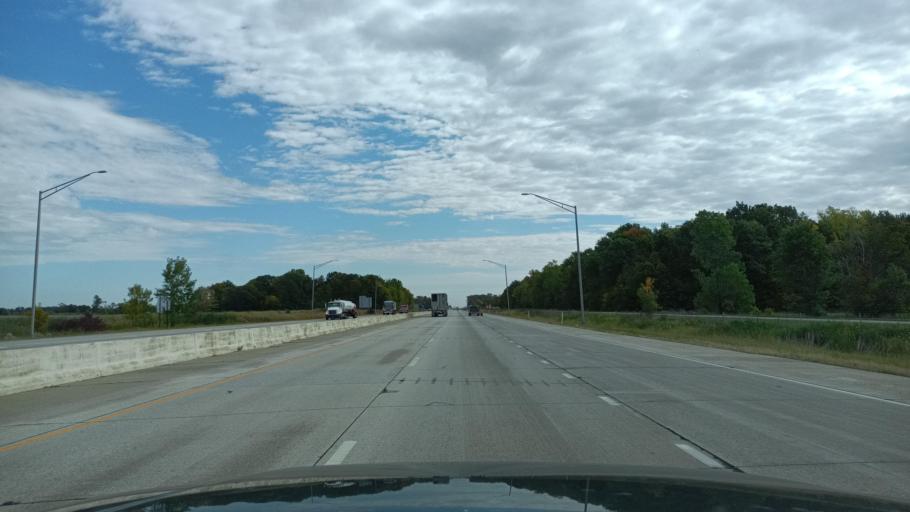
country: US
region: Indiana
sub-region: Wells County
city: Ossian
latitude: 40.9548
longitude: -85.1631
